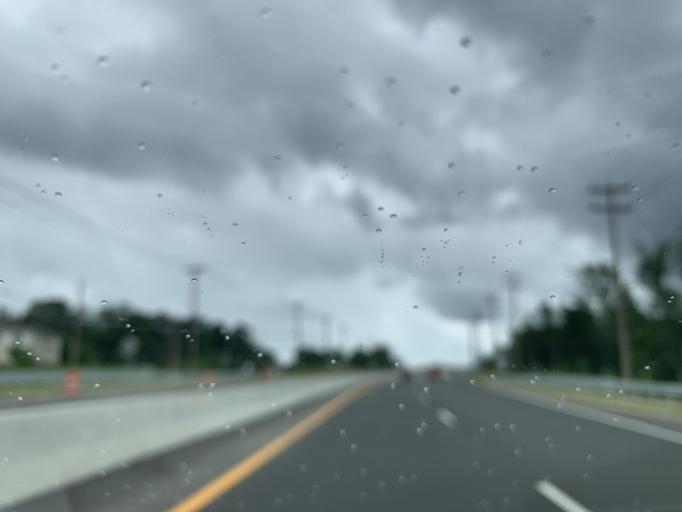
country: US
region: New Jersey
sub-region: Somerset County
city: Bloomingdale
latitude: 40.5117
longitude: -74.6327
